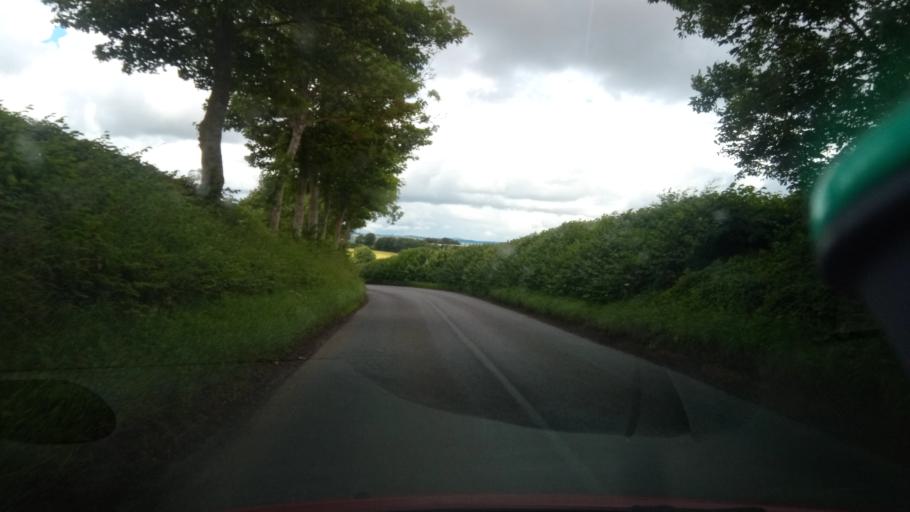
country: GB
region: Scotland
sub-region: The Scottish Borders
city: Kelso
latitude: 55.5803
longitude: -2.4205
